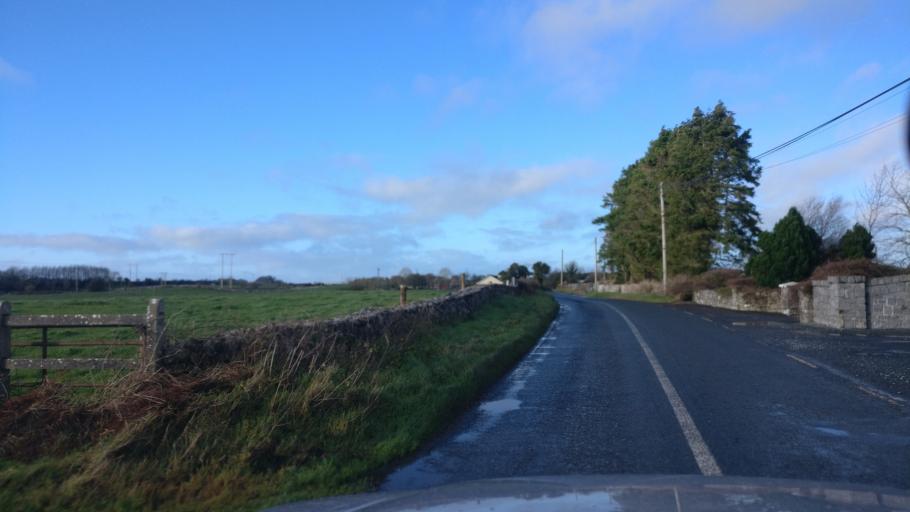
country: IE
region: Connaught
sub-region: County Galway
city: Athenry
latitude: 53.2646
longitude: -8.6875
